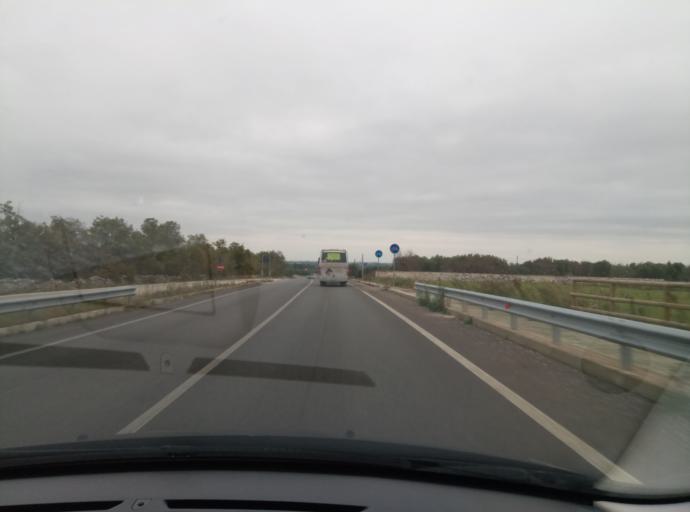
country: IT
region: Apulia
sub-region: Provincia di Bari
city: Acquaviva delle Fonti
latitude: 40.8729
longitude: 16.8069
